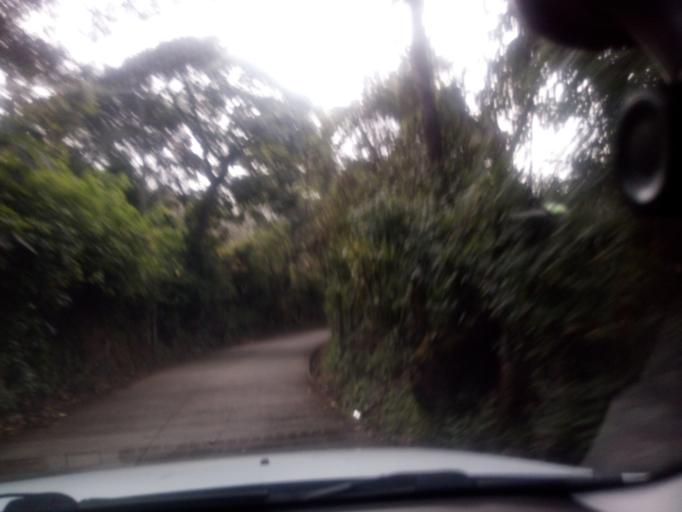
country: GT
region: Sacatepequez
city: San Bartolome Milpas Altas
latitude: 14.5997
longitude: -90.6793
